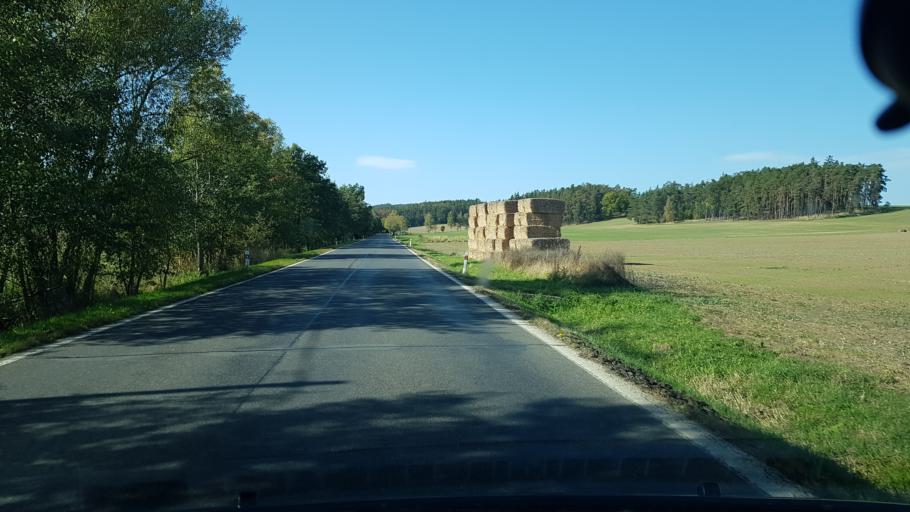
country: CZ
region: Jihocesky
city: Radomysl
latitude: 49.2957
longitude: 14.0247
